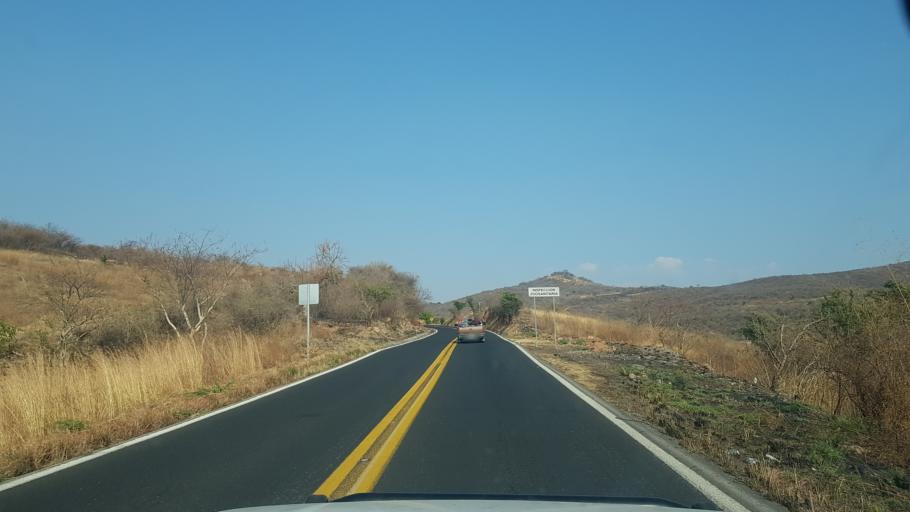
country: MX
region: Puebla
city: Calmeca
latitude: 18.6417
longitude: -98.6135
